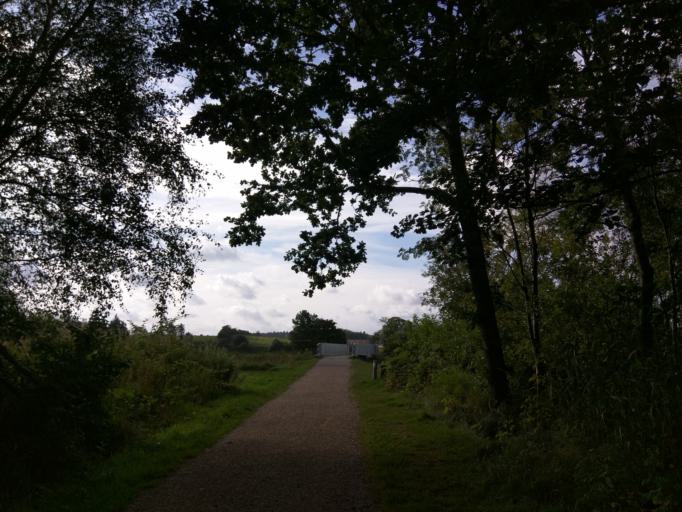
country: DK
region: Central Jutland
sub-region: Viborg Kommune
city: Viborg
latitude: 56.4362
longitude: 9.4194
